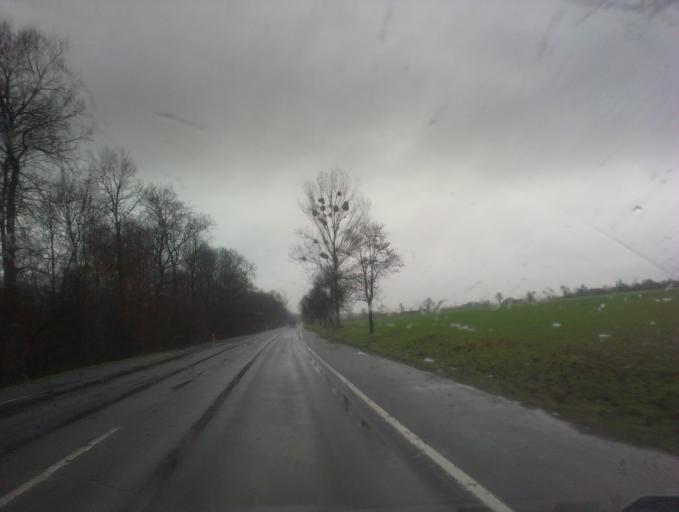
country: PL
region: Greater Poland Voivodeship
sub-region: Powiat obornicki
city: Oborniki
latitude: 52.6857
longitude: 16.8780
